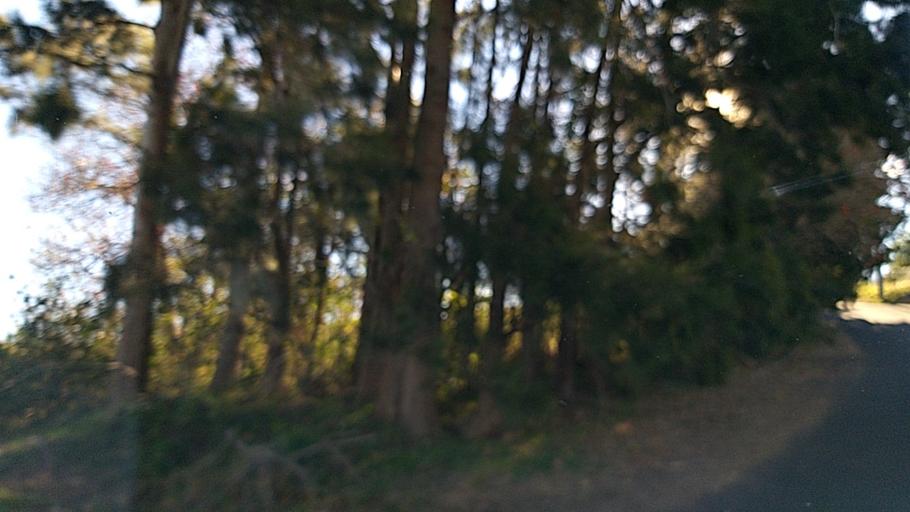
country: AU
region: New South Wales
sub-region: Wollongong
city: Mount Keira
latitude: -34.4233
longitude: 150.8412
